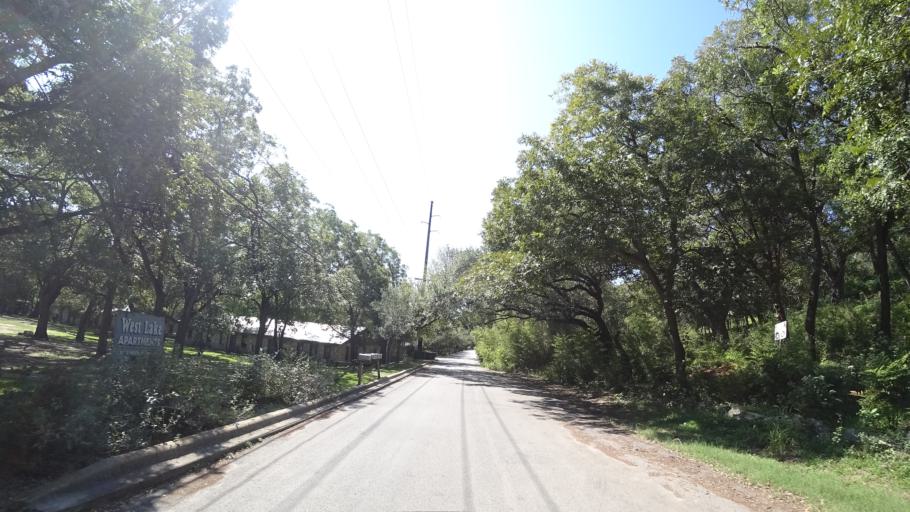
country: US
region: Texas
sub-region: Travis County
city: West Lake Hills
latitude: 30.3060
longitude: -97.7825
